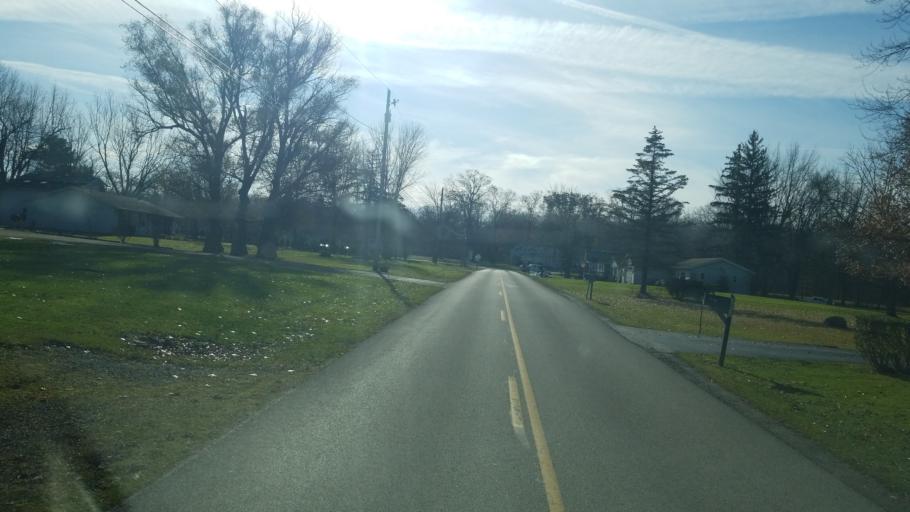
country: US
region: Ohio
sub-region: Ashtabula County
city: Jefferson
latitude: 41.7504
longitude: -80.7898
